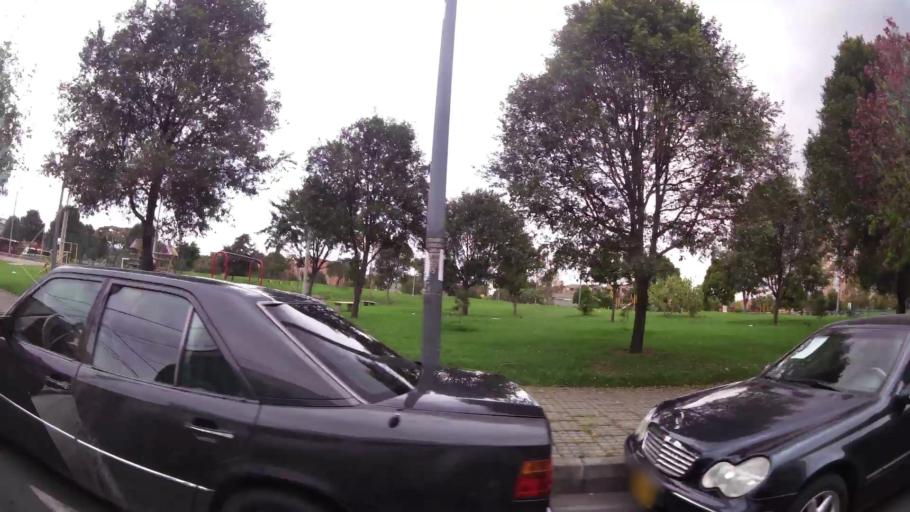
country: CO
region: Bogota D.C.
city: Barrio San Luis
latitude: 4.6896
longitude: -74.0790
